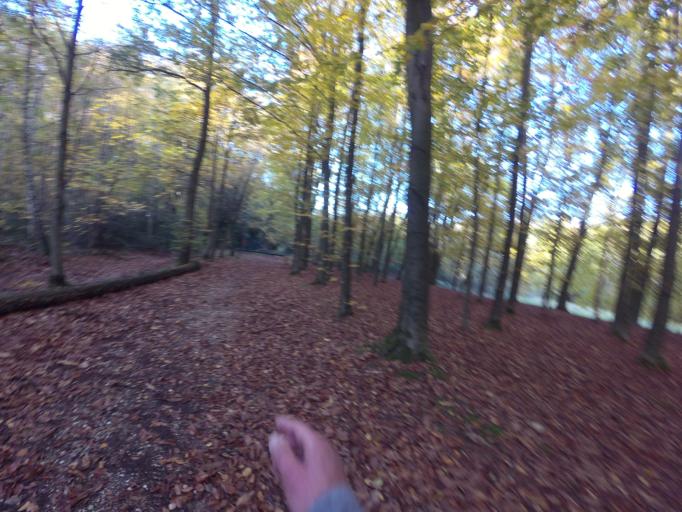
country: BE
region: Wallonia
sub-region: Province de Liege
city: Plombieres
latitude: 50.7817
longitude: 5.9397
